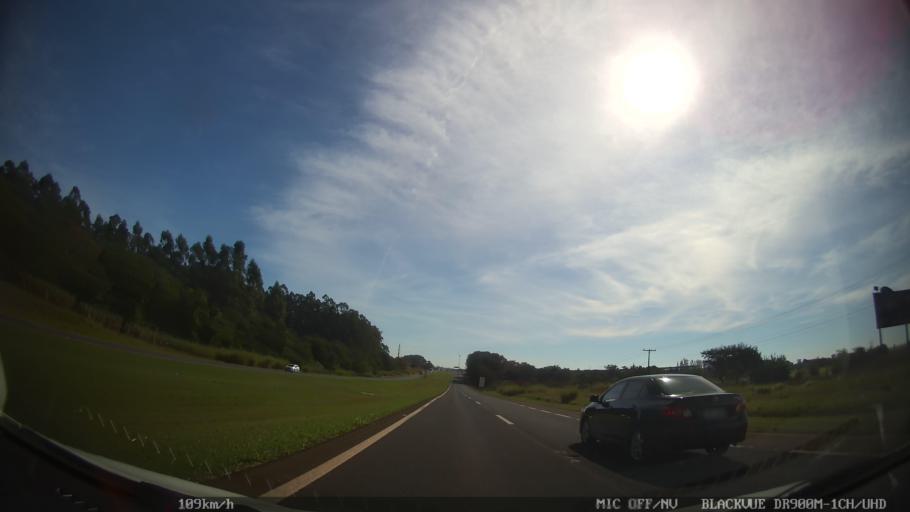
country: BR
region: Sao Paulo
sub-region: Leme
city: Leme
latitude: -22.2316
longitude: -47.3911
